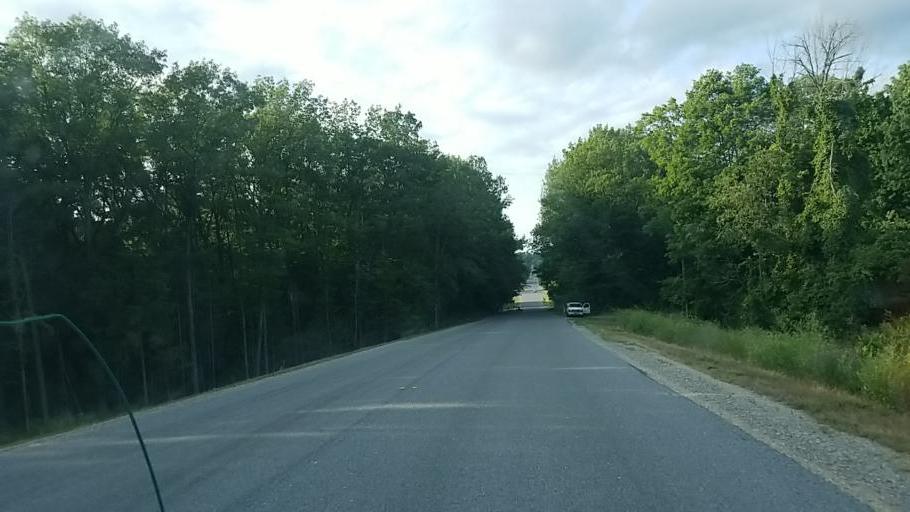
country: US
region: Michigan
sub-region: Ionia County
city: Belding
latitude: 43.0686
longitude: -85.3523
